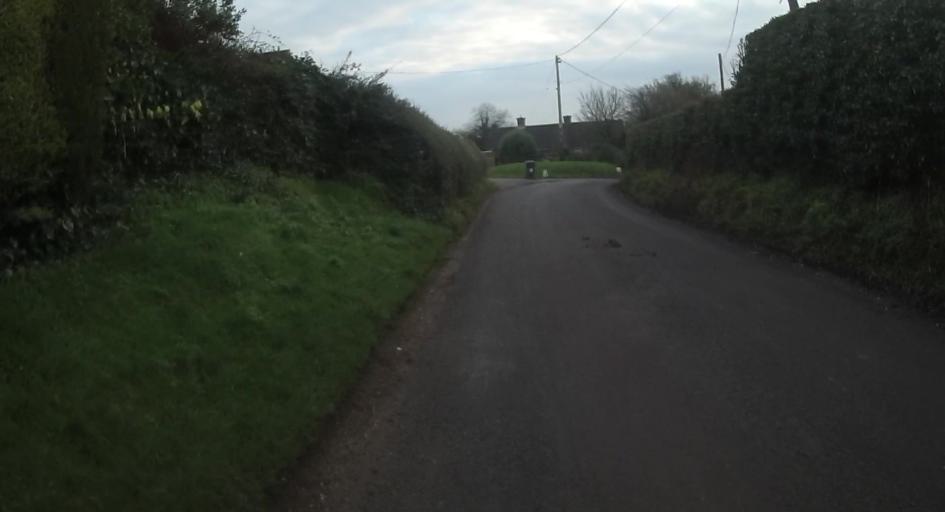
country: GB
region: England
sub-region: Hampshire
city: Kingsclere
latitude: 51.2937
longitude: -1.2264
